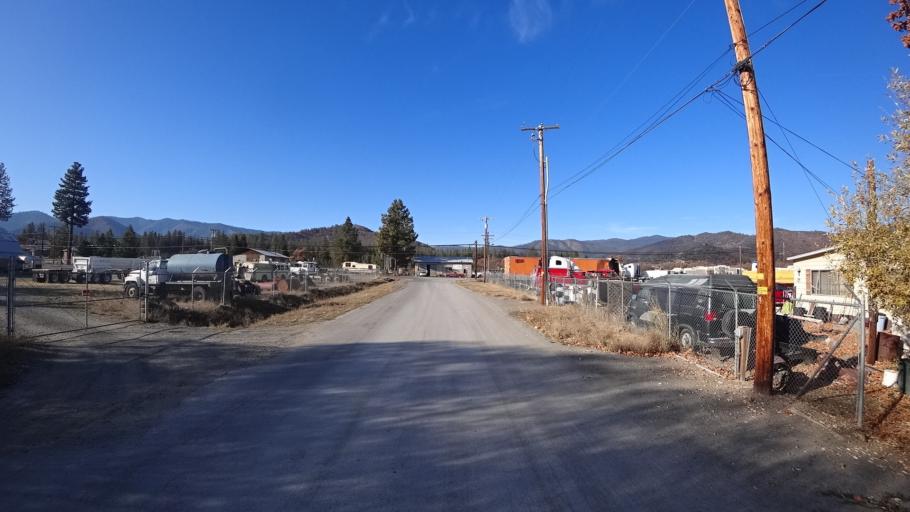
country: US
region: California
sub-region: Siskiyou County
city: Yreka
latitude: 41.6917
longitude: -122.6364
